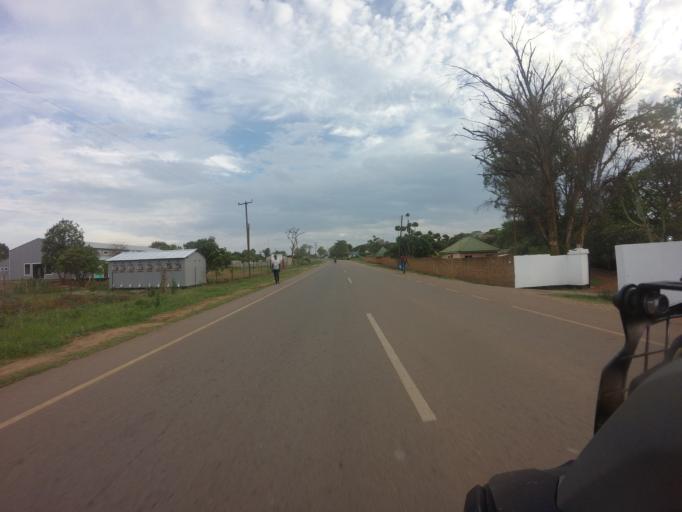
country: ZM
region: Lusaka
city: Lusaka
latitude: -15.5220
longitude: 28.2347
